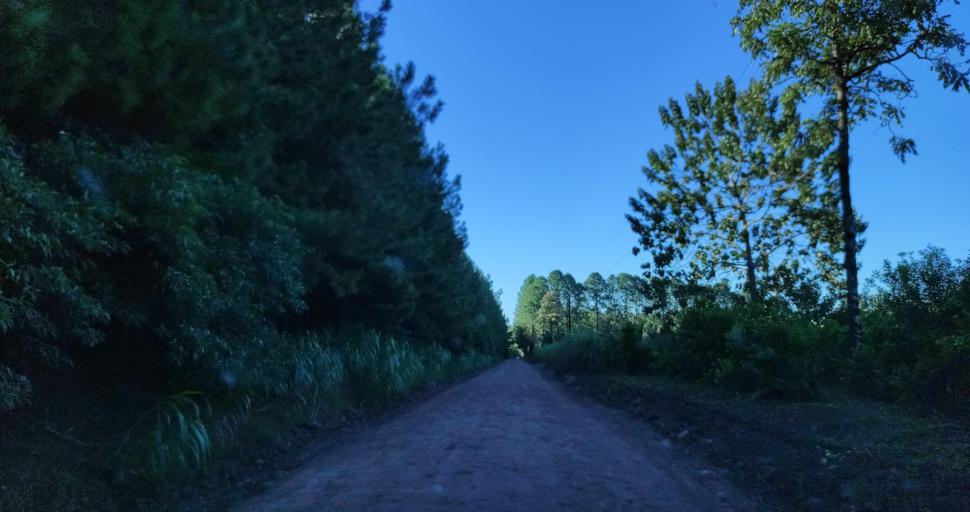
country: AR
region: Misiones
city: Garuhape
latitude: -26.8793
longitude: -54.9961
